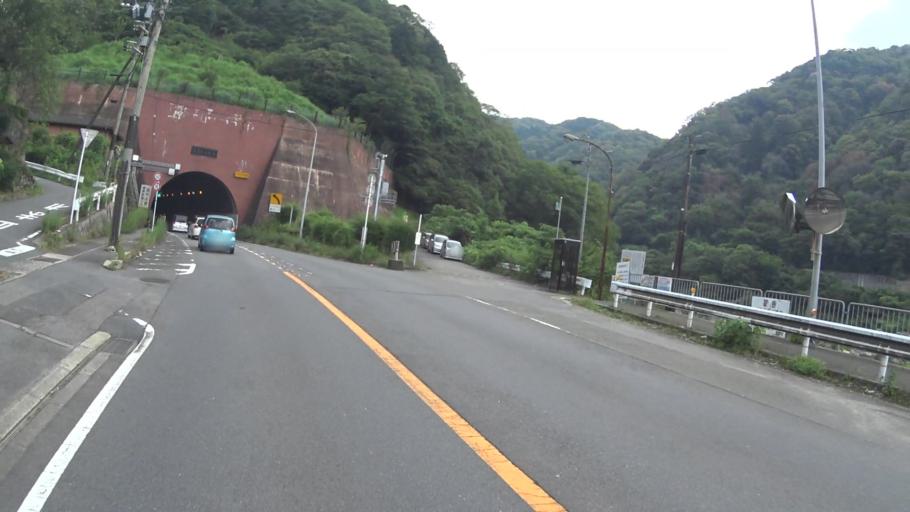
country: JP
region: Nara
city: Nara-shi
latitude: 34.7596
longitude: 135.9407
